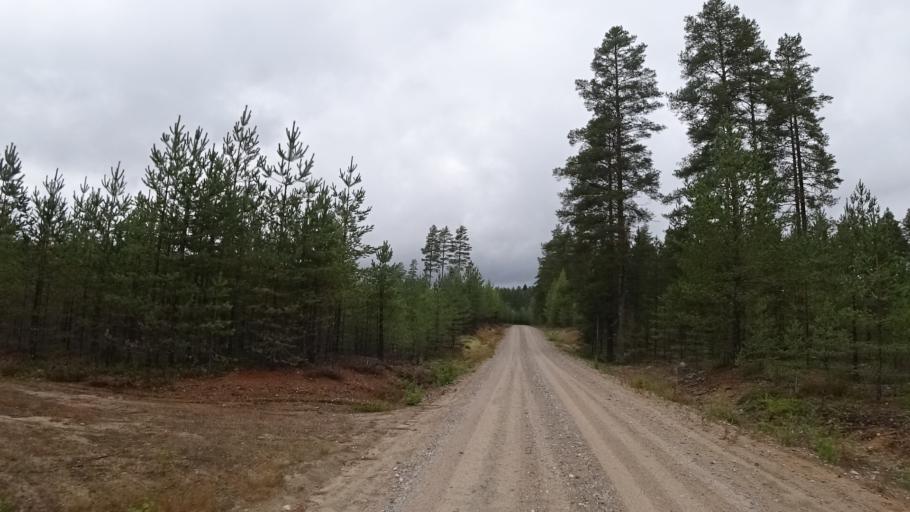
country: FI
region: North Karelia
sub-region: Pielisen Karjala
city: Lieksa
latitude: 63.5290
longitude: 30.0707
